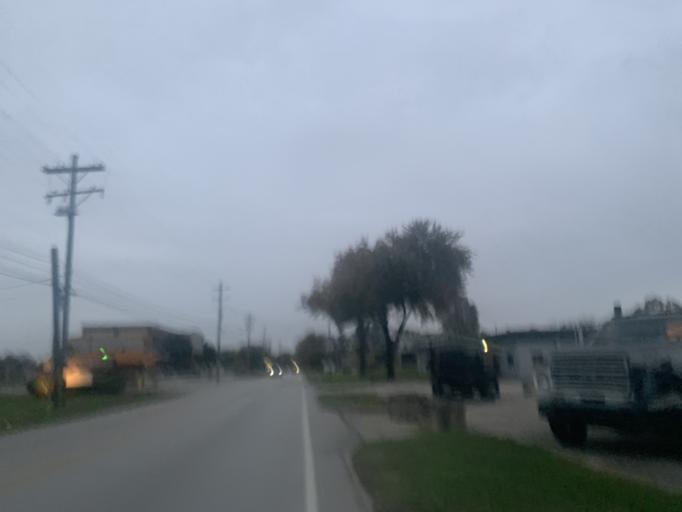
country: US
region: Kentucky
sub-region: Jefferson County
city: Shively
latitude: 38.2154
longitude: -85.8058
